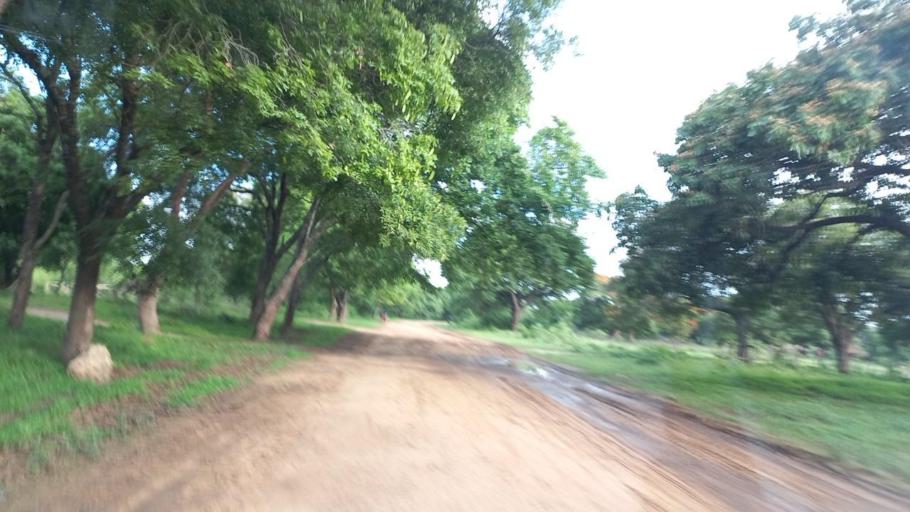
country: ZM
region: North-Western
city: Kabompo
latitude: -13.3752
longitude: 24.2989
